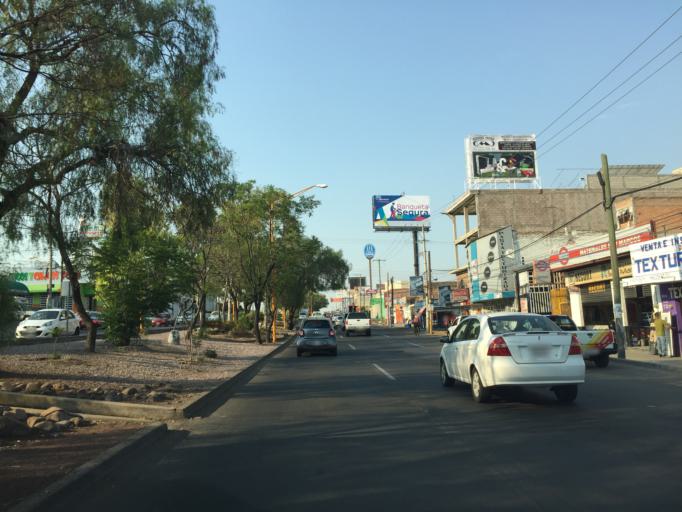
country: MX
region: Aguascalientes
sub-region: Aguascalientes
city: La Loma de los Negritos
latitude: 21.8780
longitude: -102.3182
